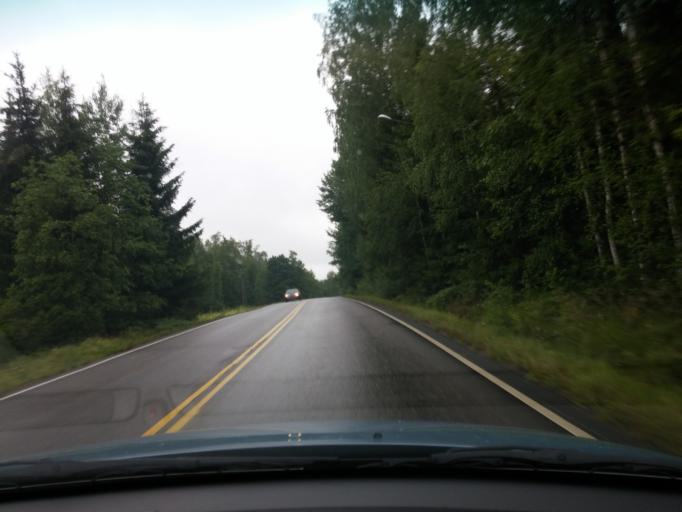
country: FI
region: Uusimaa
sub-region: Helsinki
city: Nurmijaervi
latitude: 60.3558
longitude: 24.7450
